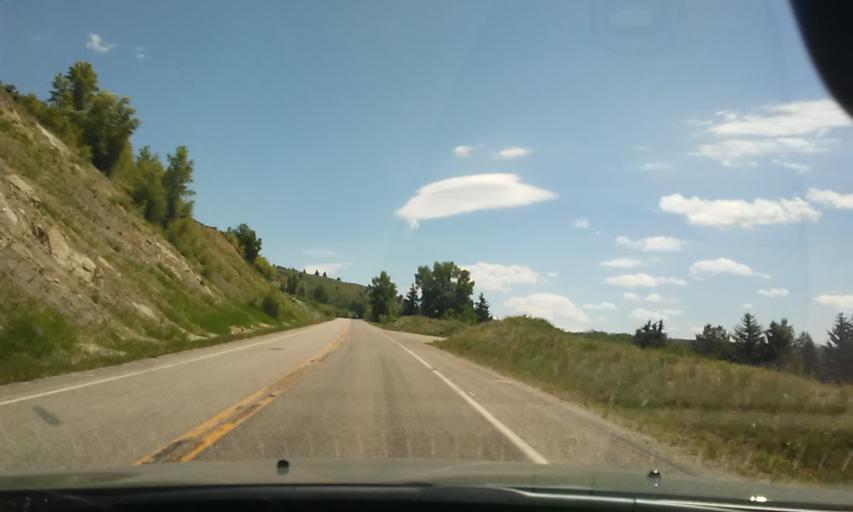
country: US
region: Wyoming
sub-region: Teton County
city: Jackson
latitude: 43.8375
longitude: -110.4978
